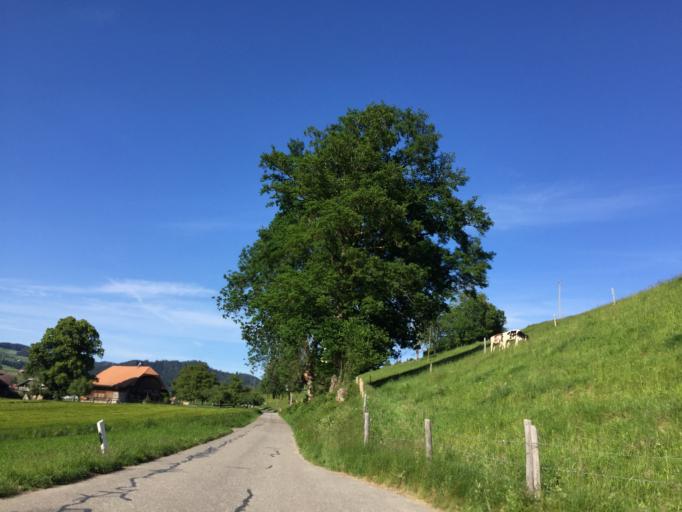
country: CH
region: Bern
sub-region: Bern-Mittelland District
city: Konolfingen
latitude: 46.8843
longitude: 7.6410
